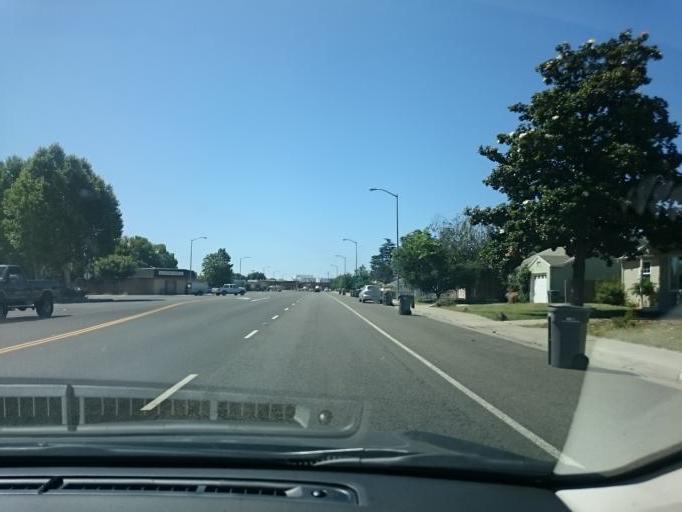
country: US
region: California
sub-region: Yolo County
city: West Sacramento
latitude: 38.5747
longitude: -121.5244
